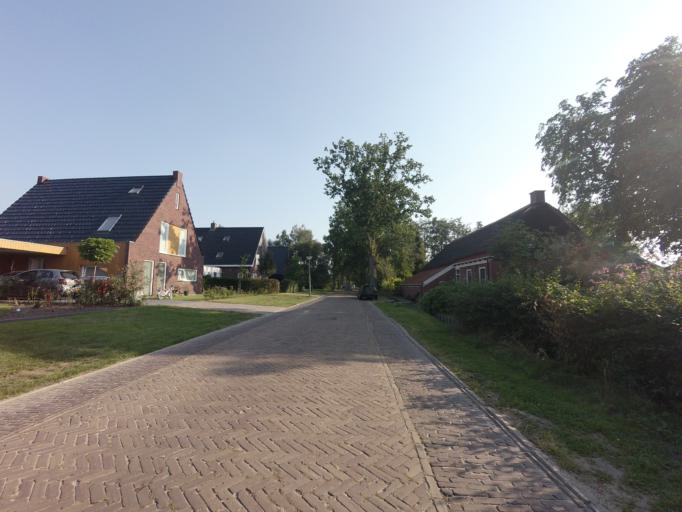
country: NL
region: Groningen
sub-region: Gemeente Groningen
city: Groningen
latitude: 53.1436
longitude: 6.4888
